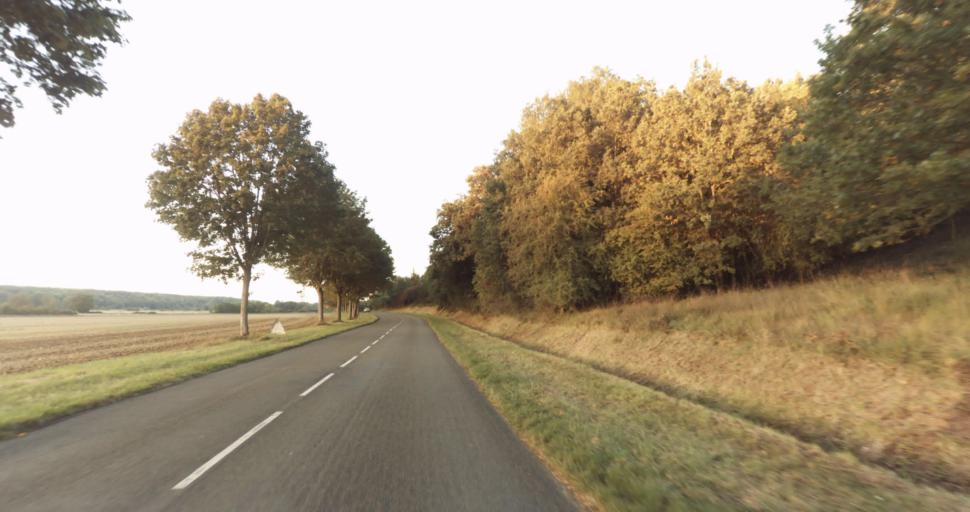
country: FR
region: Centre
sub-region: Departement d'Eure-et-Loir
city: Garnay
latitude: 48.7166
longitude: 1.3458
